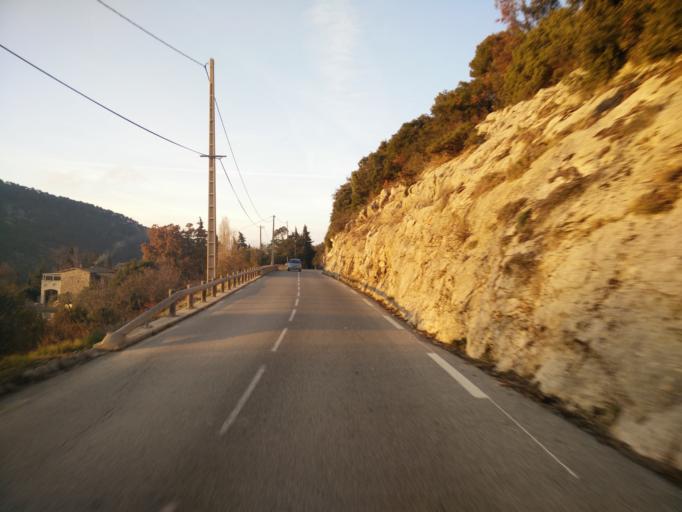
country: FR
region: Provence-Alpes-Cote d'Azur
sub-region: Departement des Alpes-Maritimes
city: Peille
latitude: 43.7850
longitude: 7.4072
